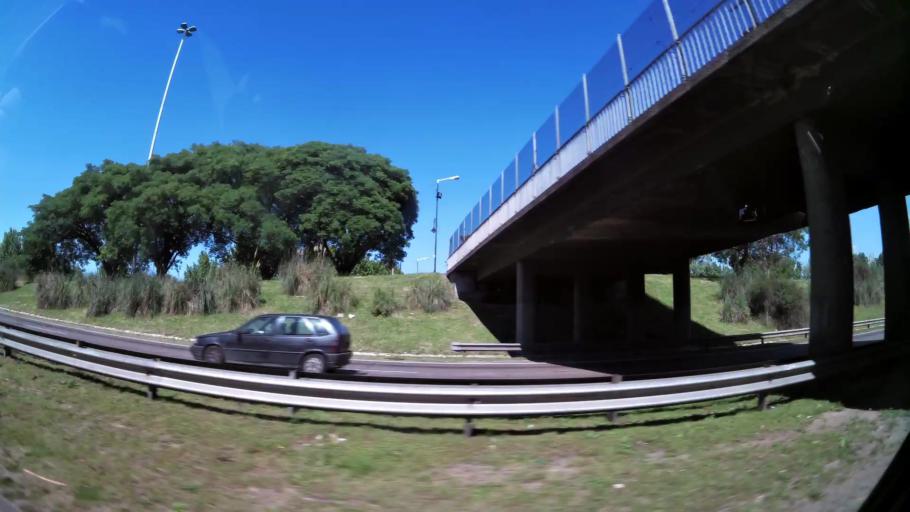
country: AR
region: Buenos Aires
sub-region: Partido de Tigre
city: Tigre
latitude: -34.4655
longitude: -58.5701
